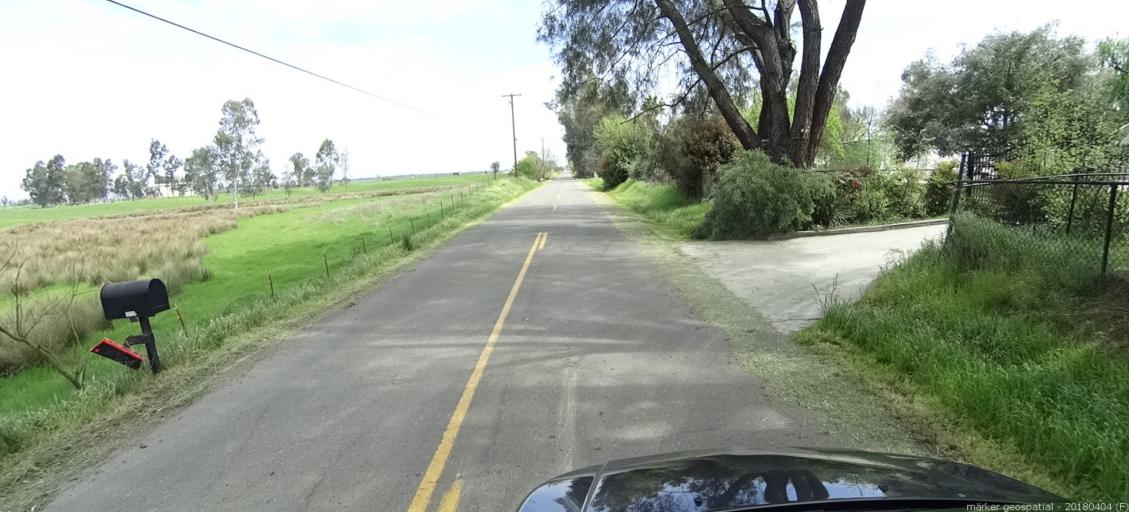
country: US
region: California
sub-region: Sacramento County
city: Herald
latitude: 38.3067
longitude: -121.2232
